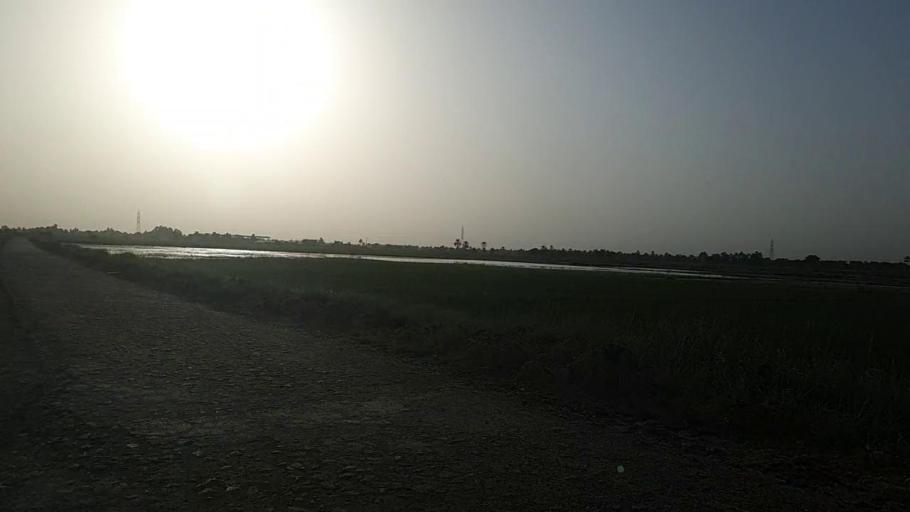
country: PK
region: Sindh
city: Naushahro Firoz
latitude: 26.8087
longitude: 68.1115
